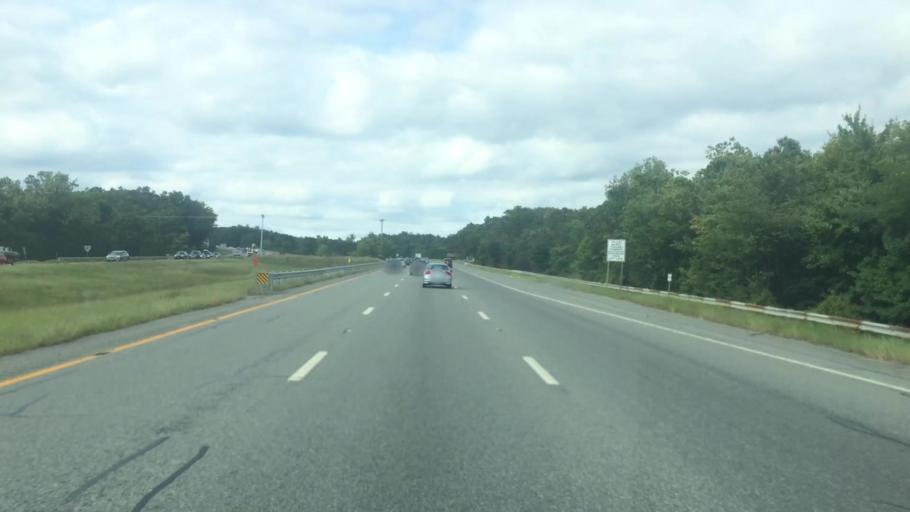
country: US
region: Rhode Island
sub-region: Providence County
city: Greenville
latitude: 41.8746
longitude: -71.5149
